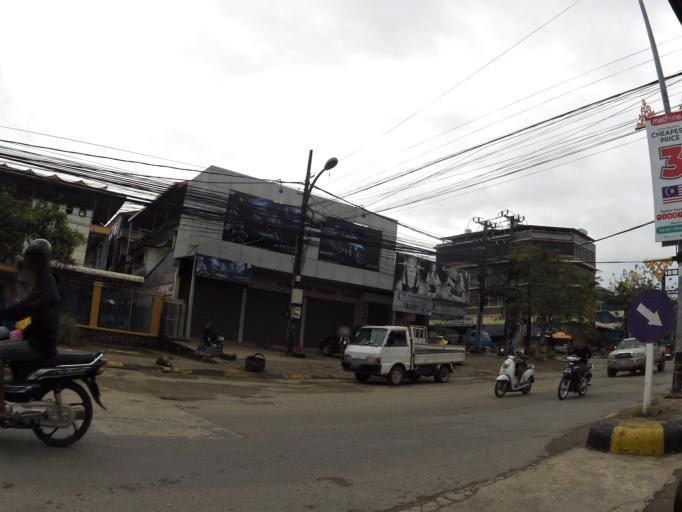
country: KH
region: Preah Sihanouk
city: Sihanoukville
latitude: 10.6244
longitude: 103.5210
